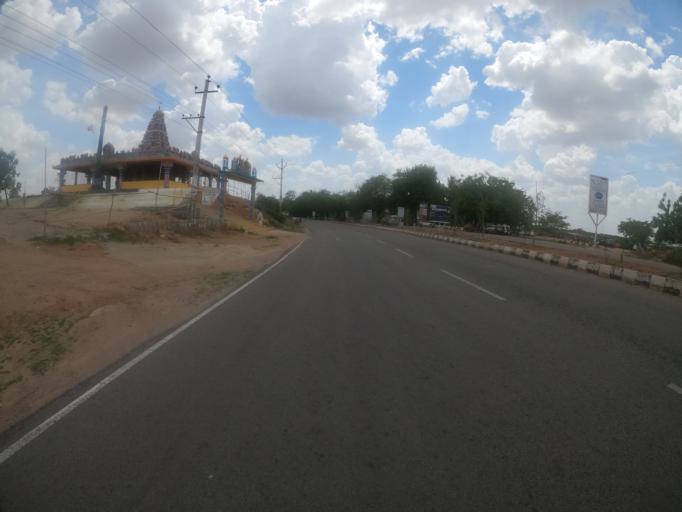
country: IN
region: Telangana
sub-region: Rangareddi
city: Sriramnagar
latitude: 17.3312
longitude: 78.2890
